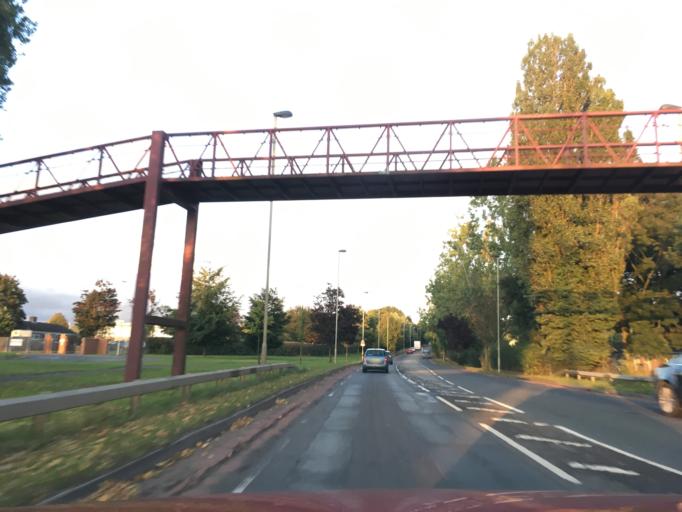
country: GB
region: England
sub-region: Gloucestershire
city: Gloucester
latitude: 51.8381
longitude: -2.2565
